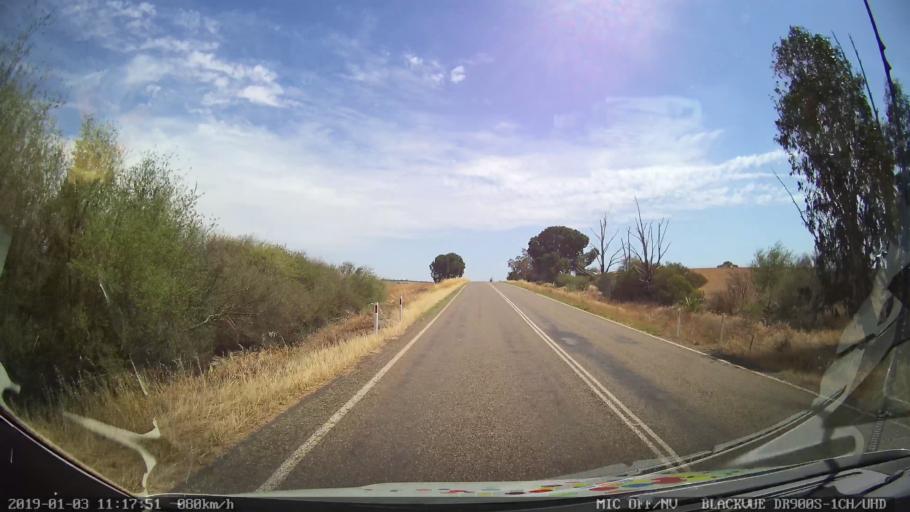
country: AU
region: New South Wales
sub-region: Young
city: Young
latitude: -34.1336
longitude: 148.2643
